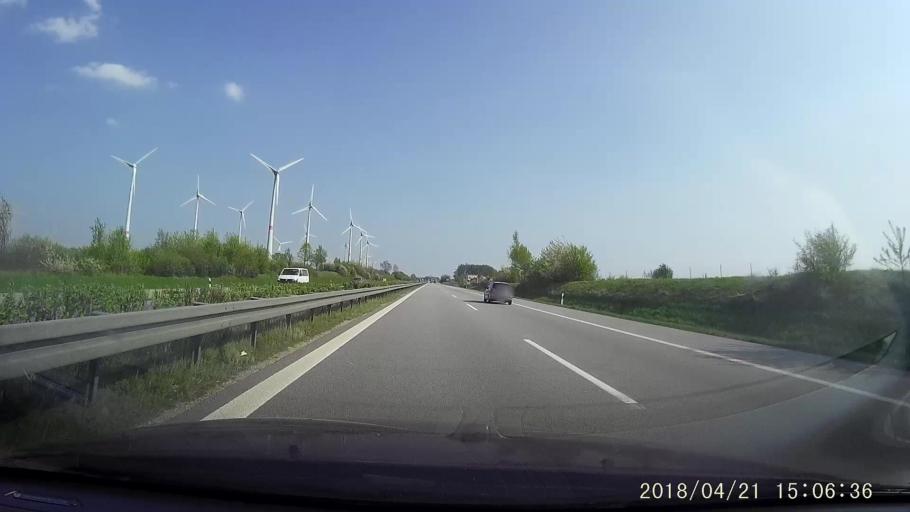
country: DE
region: Saxony
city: Kodersdorf
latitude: 51.2109
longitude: 14.9398
